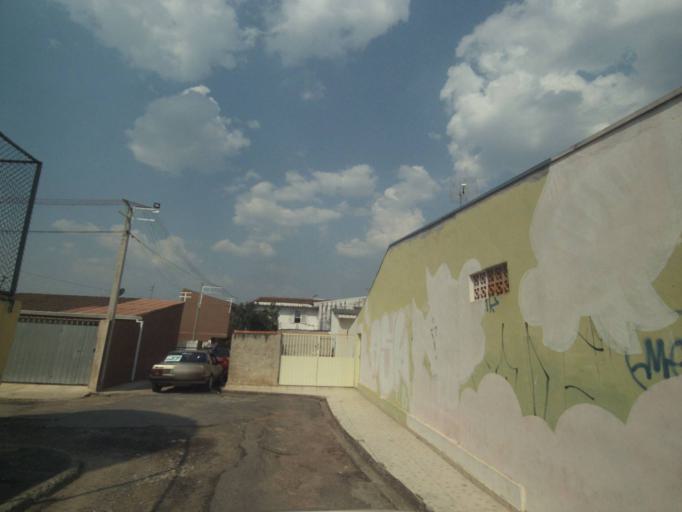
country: BR
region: Parana
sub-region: Sao Jose Dos Pinhais
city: Sao Jose dos Pinhais
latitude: -25.5382
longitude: -49.2383
